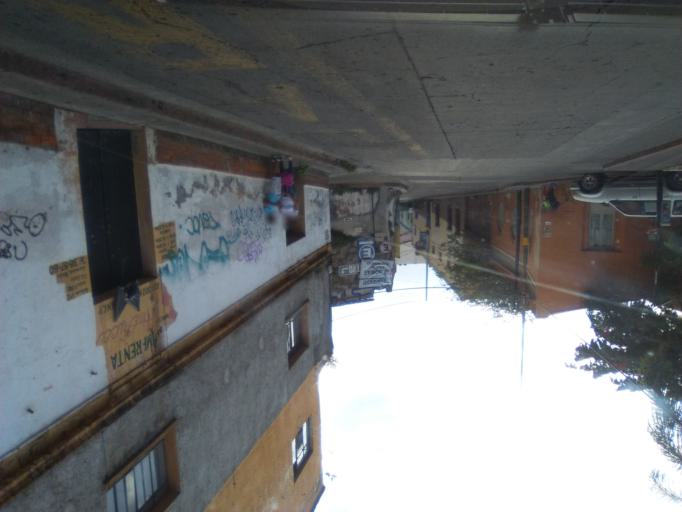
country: MX
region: Morelos
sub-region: Cuernavaca
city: Cuernavaca
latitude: 18.9221
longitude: -99.2317
